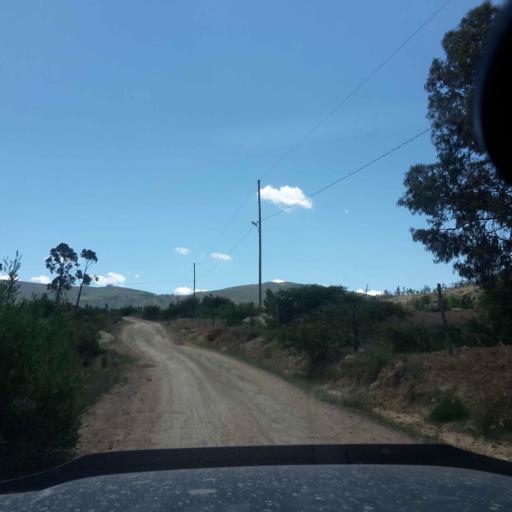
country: BO
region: Cochabamba
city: Totora
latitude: -17.7728
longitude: -65.2455
